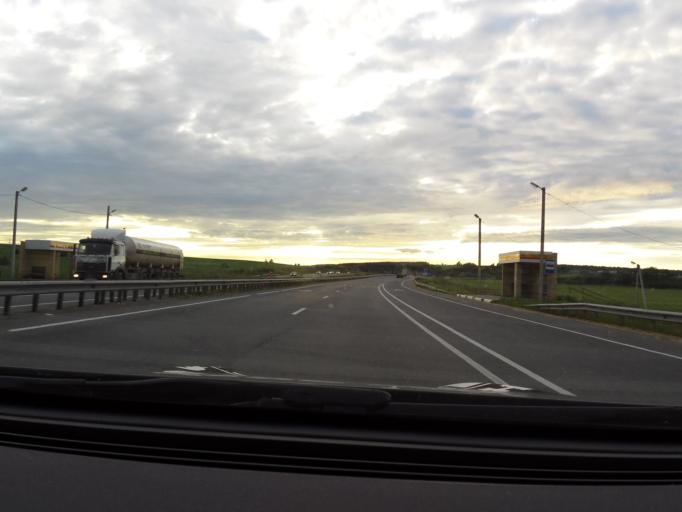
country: RU
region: Chuvashia
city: Kugesi
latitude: 55.9779
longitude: 47.3572
